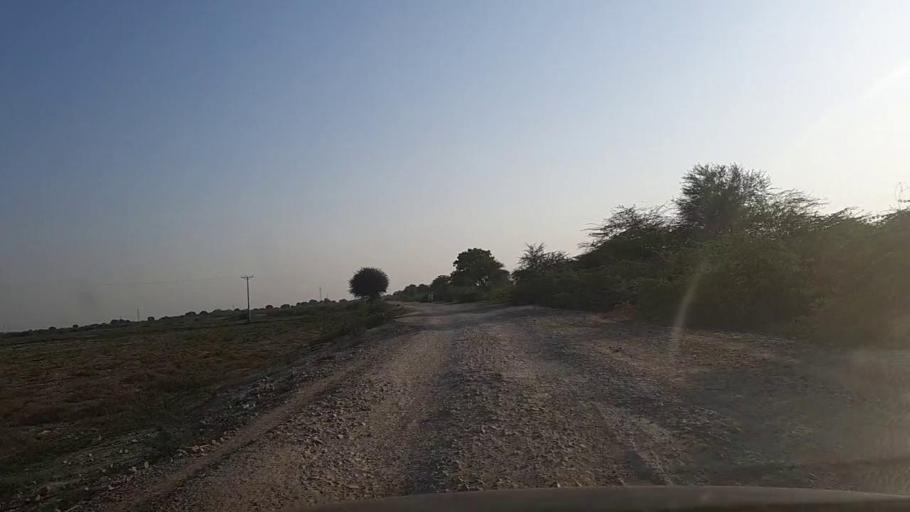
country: PK
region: Sindh
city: Naukot
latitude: 24.8957
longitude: 69.3353
